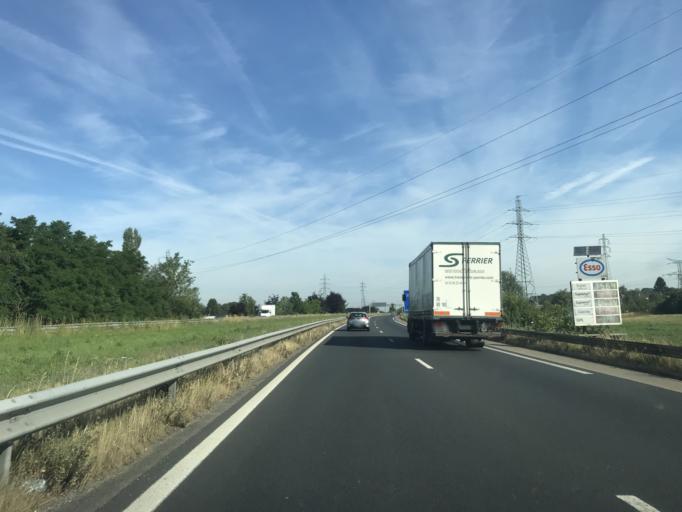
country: FR
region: Haute-Normandie
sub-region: Departement de la Seine-Maritime
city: La Vaupaliere
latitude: 49.4862
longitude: 1.0024
